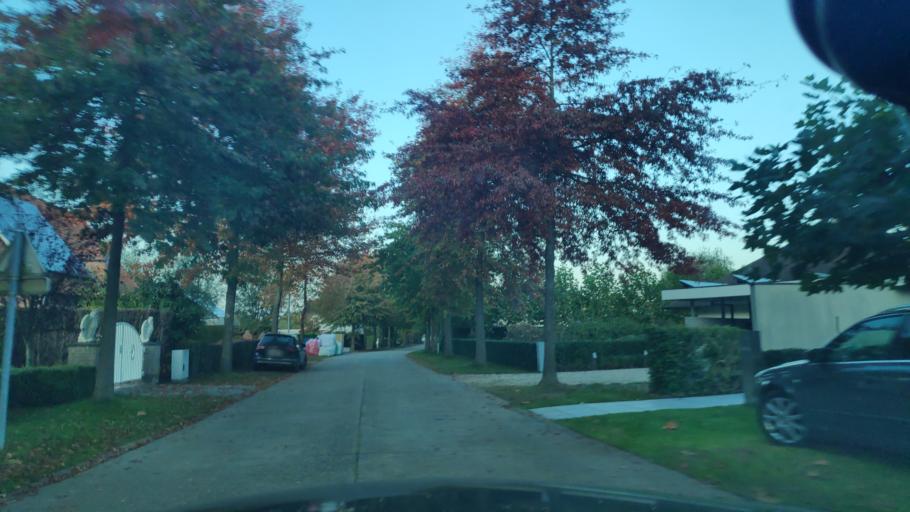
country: BE
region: Flanders
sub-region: Provincie Oost-Vlaanderen
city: Aalter
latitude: 51.0941
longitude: 3.4913
